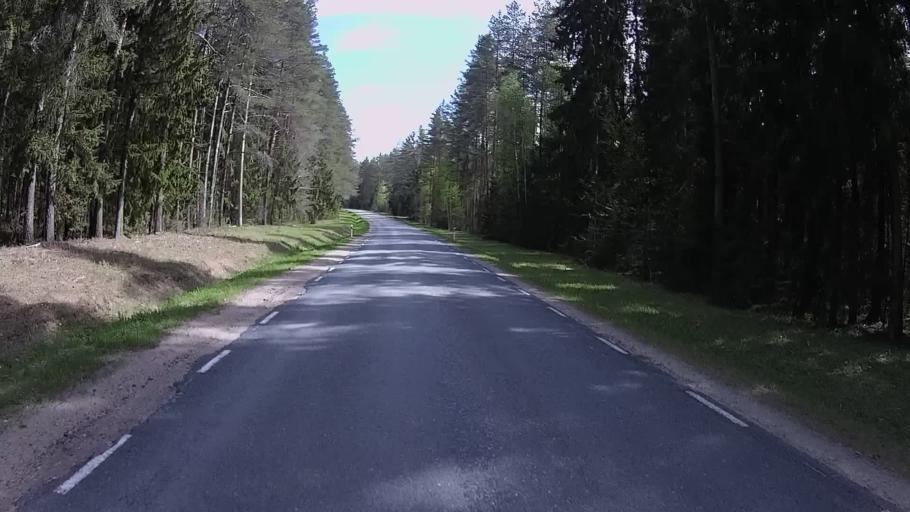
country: LV
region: Apes Novads
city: Ape
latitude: 57.6036
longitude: 26.4831
